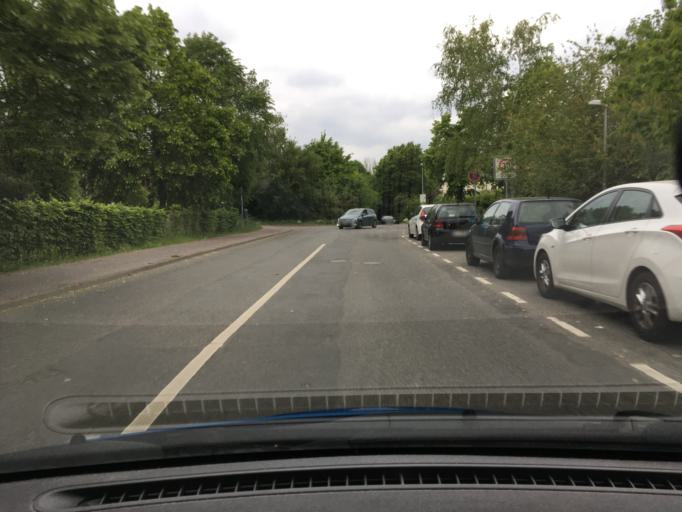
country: DE
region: Lower Saxony
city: Lueneburg
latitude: 53.2497
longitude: 10.3842
